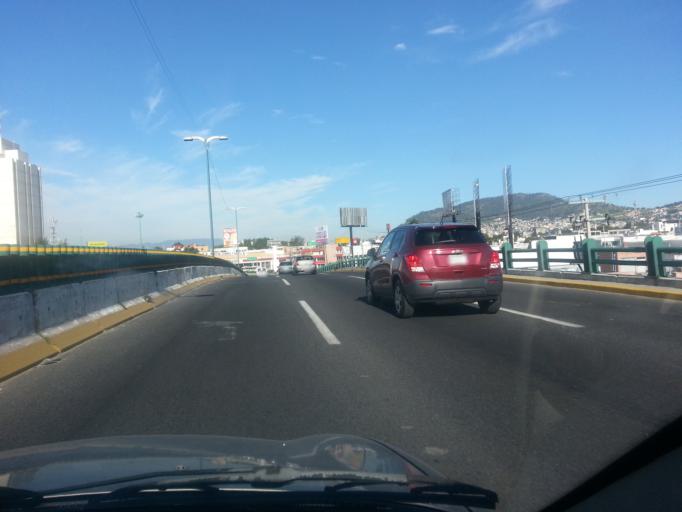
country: MX
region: Mexico
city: Toluca
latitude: 19.2840
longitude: -99.6378
